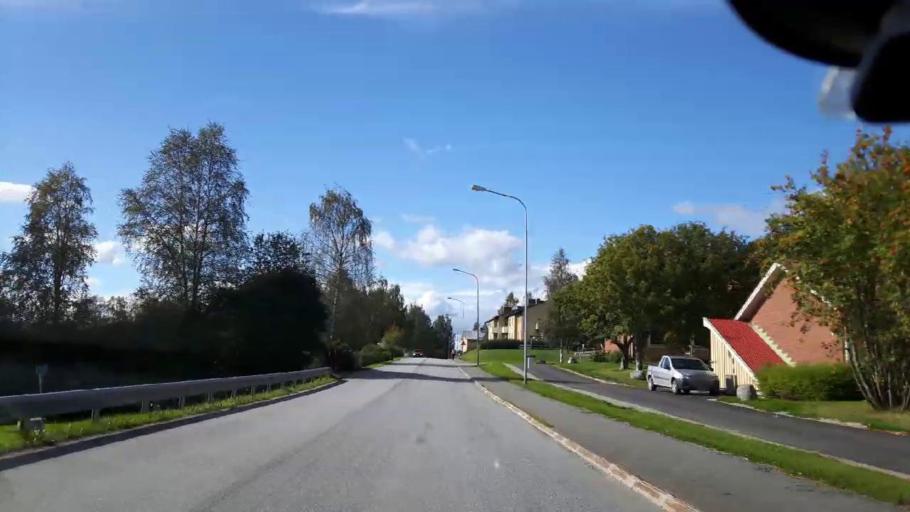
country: SE
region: Jaemtland
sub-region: Braecke Kommun
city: Braecke
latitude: 63.1688
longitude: 15.5816
